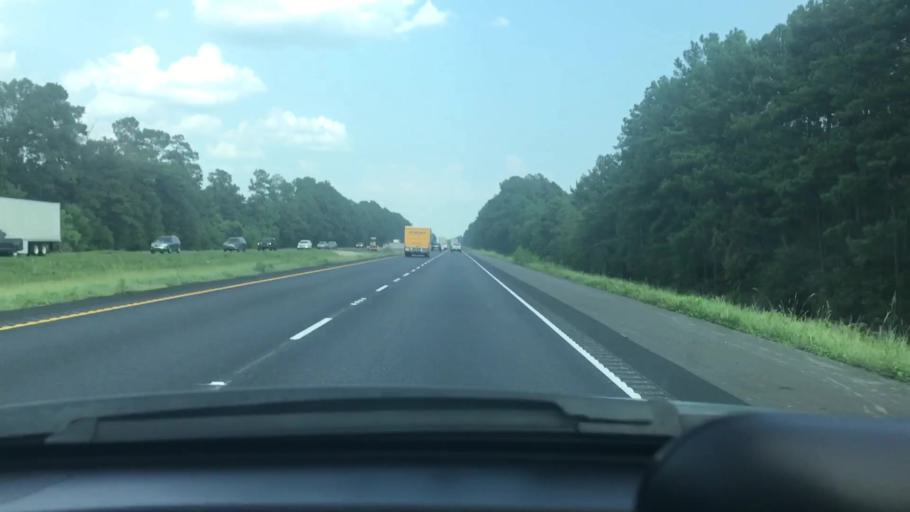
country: US
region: Louisiana
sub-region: Livingston Parish
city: Livingston
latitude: 30.4751
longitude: -90.6864
